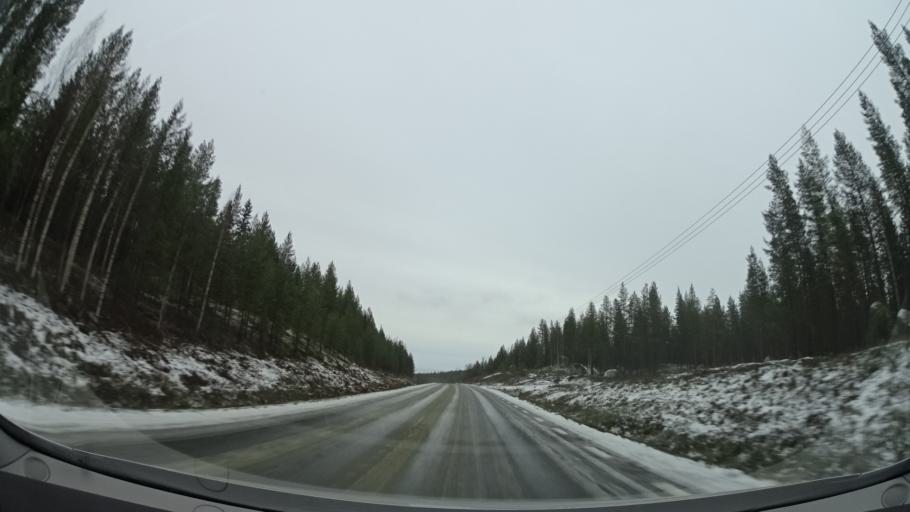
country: SE
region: Vaesterbotten
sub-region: Lycksele Kommun
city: Lycksele
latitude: 64.5679
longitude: 18.6090
